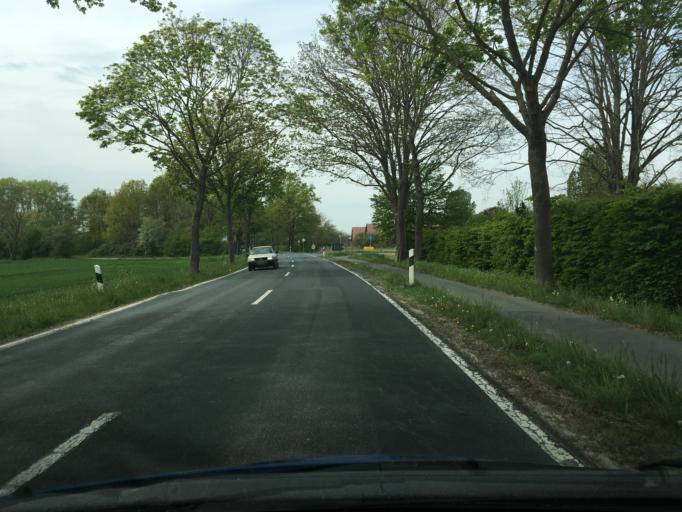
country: DE
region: Lower Saxony
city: Elze
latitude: 52.1738
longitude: 9.7218
